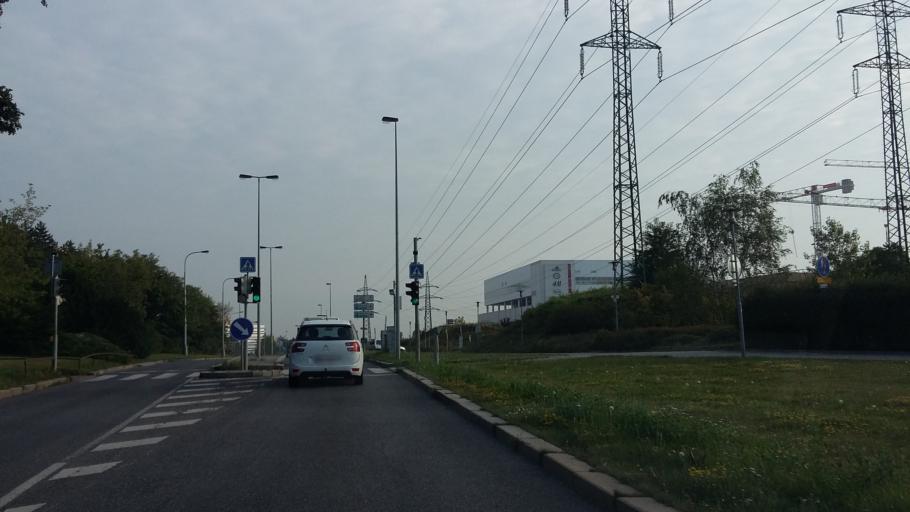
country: CZ
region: Central Bohemia
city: Vestec
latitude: 50.0286
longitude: 14.4879
